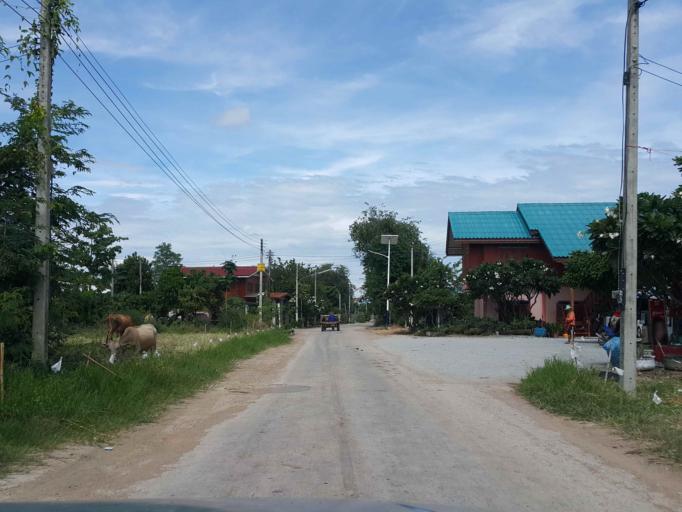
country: TH
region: Sukhothai
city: Ban Dan Lan Hoi
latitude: 17.1085
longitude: 99.4807
